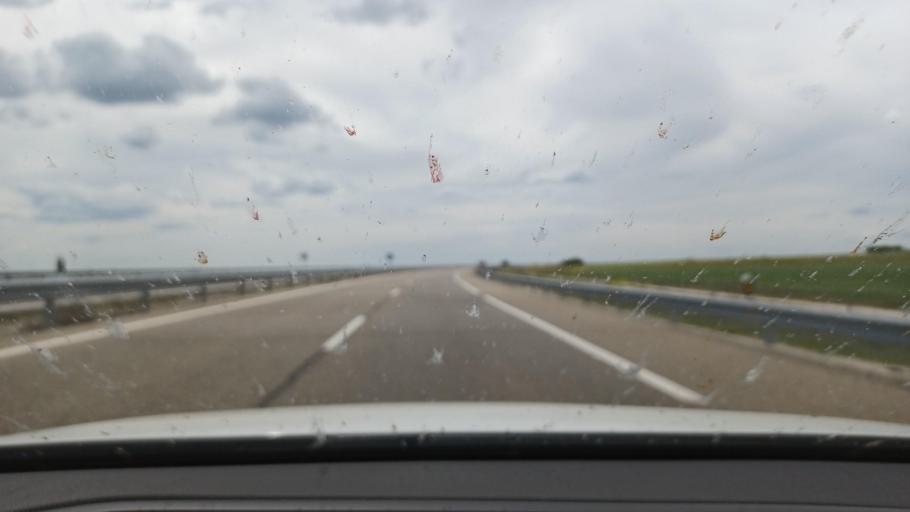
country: ES
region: Castille and Leon
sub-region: Provincia de Valladolid
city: San Miguel del Arroyo
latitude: 41.4342
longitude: -4.4320
